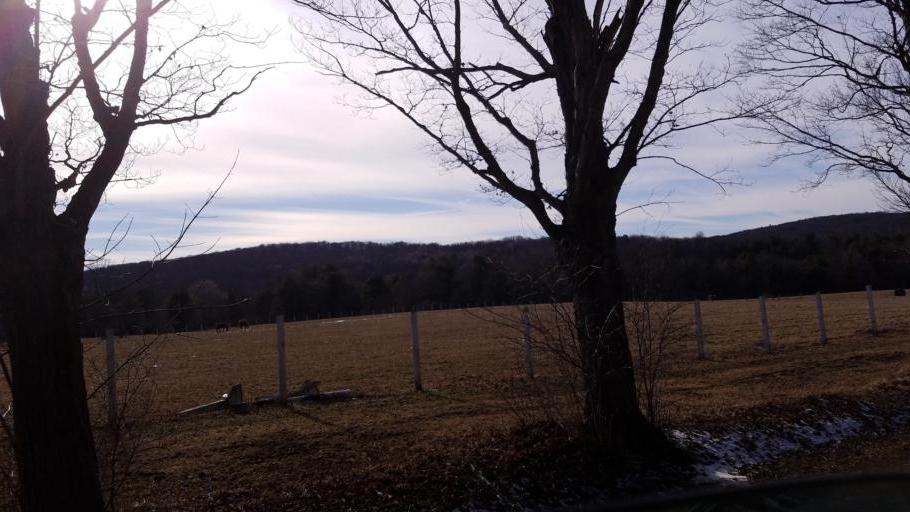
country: US
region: New York
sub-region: Allegany County
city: Wellsville
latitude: 42.0854
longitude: -78.0148
